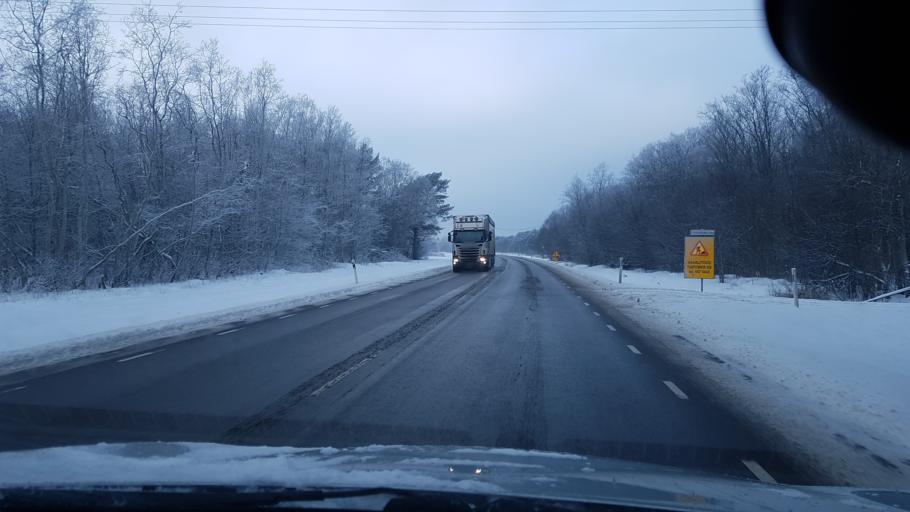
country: EE
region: Harju
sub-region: Paldiski linn
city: Paldiski
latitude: 59.3388
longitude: 24.2186
